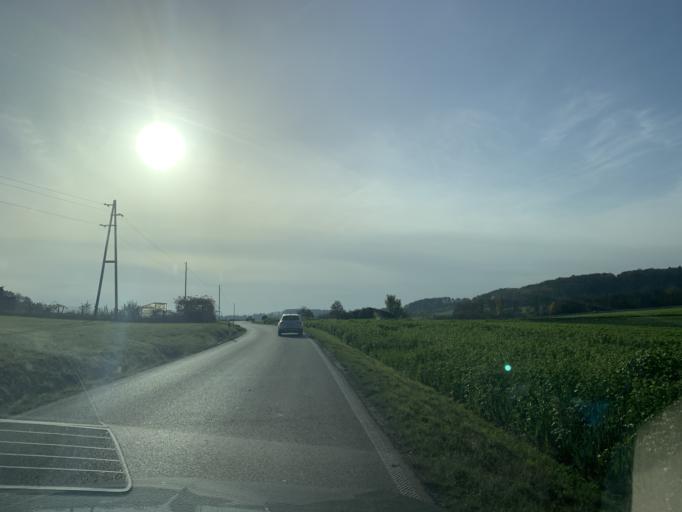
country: DE
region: Baden-Wuerttemberg
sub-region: Regierungsbezirk Stuttgart
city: Unterensingen
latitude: 48.6498
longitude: 9.3381
